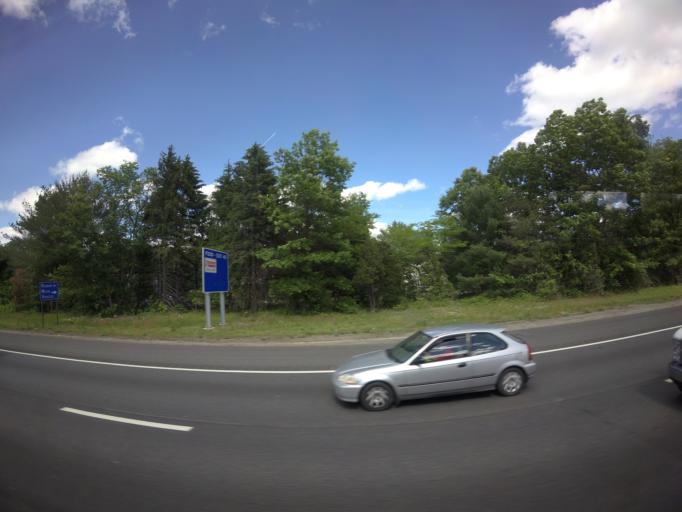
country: US
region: Massachusetts
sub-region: Middlesex County
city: Wilmington
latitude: 42.5723
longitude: -71.1486
